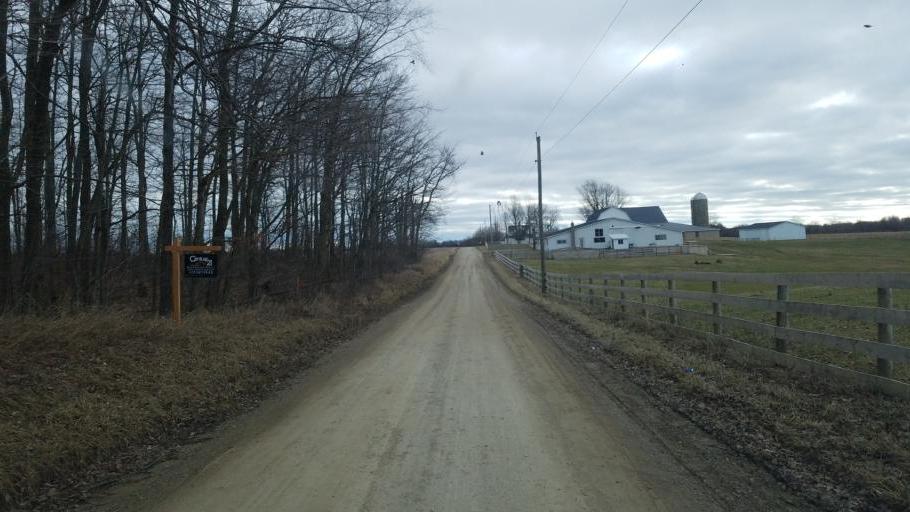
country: US
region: Ohio
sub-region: Richland County
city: Lexington
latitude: 40.5795
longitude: -82.6800
